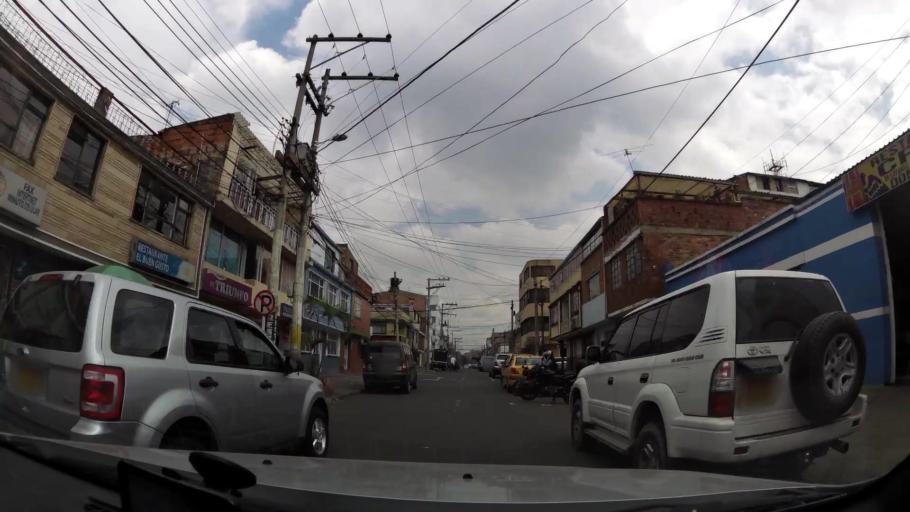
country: CO
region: Bogota D.C.
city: Barrio San Luis
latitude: 4.6813
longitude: -74.0655
